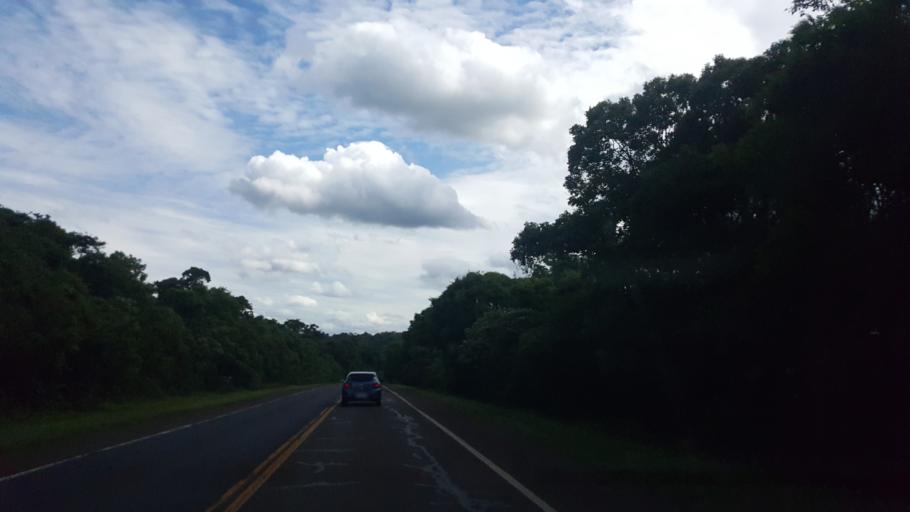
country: AR
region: Misiones
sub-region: Departamento de Iguazu
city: Puerto Iguazu
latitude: -25.7008
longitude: -54.5148
